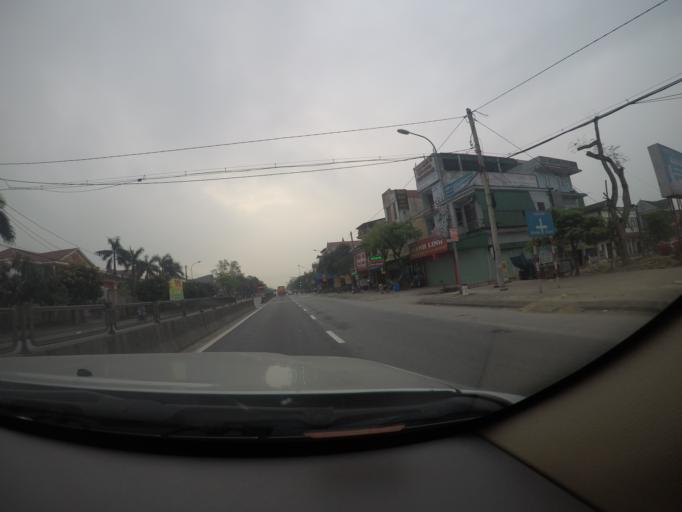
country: VN
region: Ha Tinh
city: Cam Xuyen
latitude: 18.2501
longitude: 106.0008
